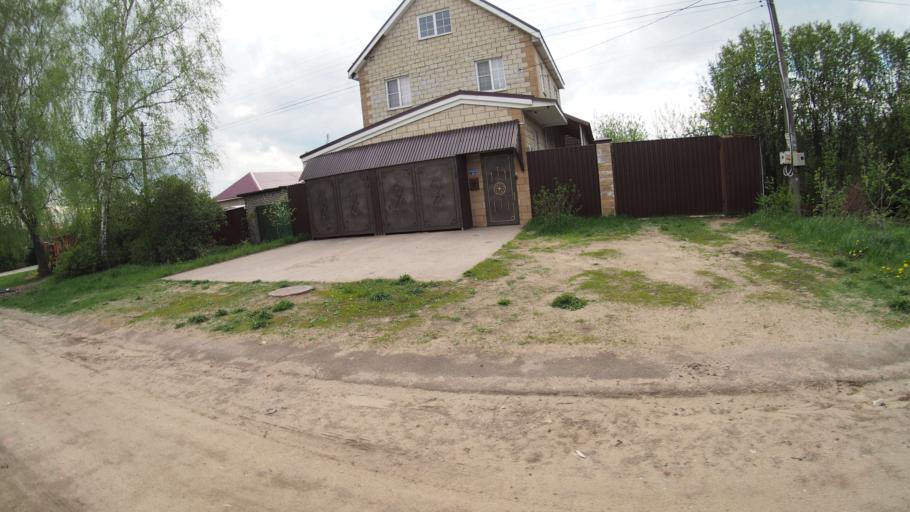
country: RU
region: Moskovskaya
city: Ramenskoye
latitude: 55.5563
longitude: 38.2342
